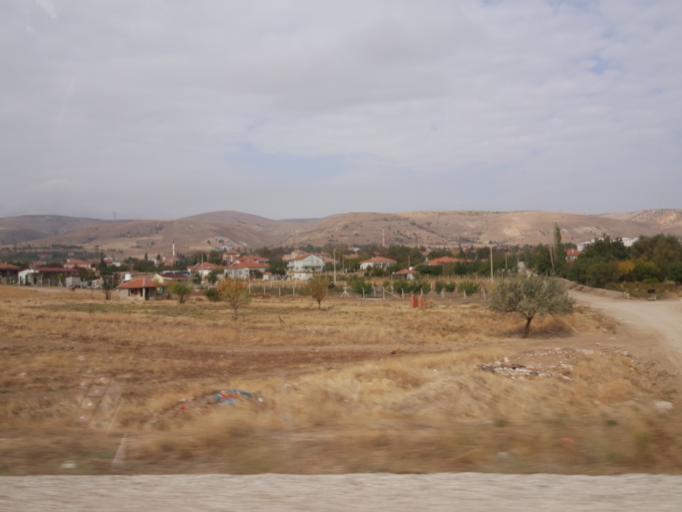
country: TR
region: Kirikkale
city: Bahsili
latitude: 39.7237
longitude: 33.4370
